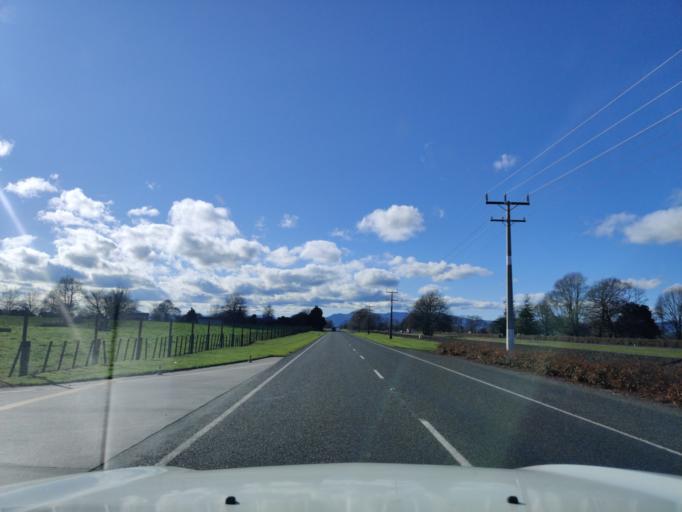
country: NZ
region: Waikato
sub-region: Matamata-Piako District
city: Matamata
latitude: -37.8484
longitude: 175.7601
